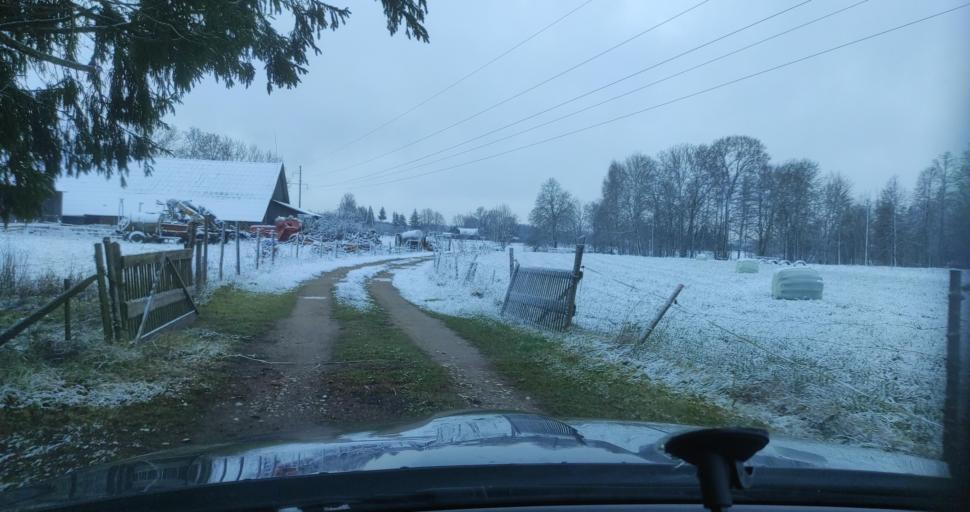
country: LV
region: Skrunda
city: Skrunda
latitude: 56.8745
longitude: 22.2329
